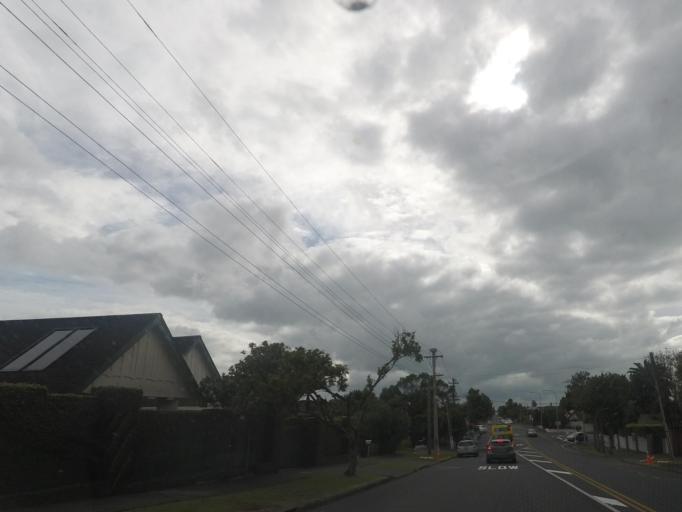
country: NZ
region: Auckland
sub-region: Auckland
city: Tamaki
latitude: -36.8667
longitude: 174.8507
